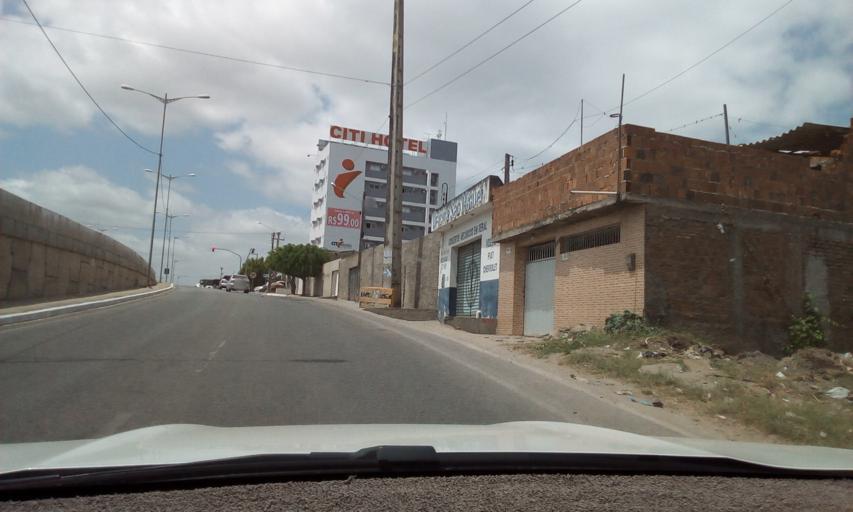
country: BR
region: Pernambuco
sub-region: Caruaru
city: Caruaru
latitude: -8.2849
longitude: -35.9838
